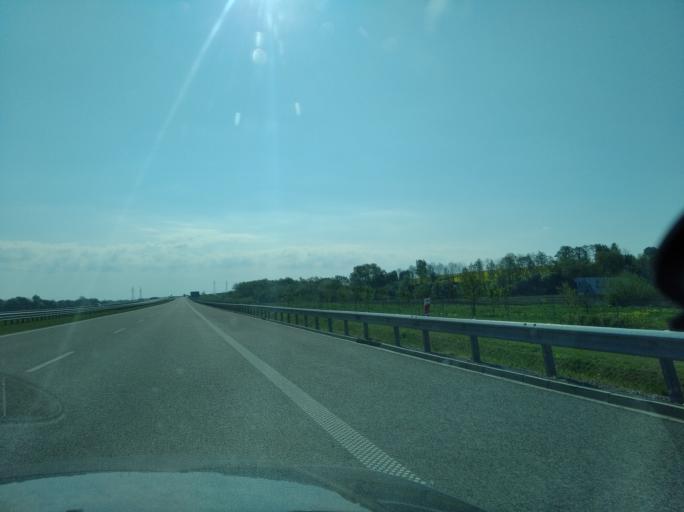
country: PL
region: Subcarpathian Voivodeship
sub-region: Powiat przemyski
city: Orly
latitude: 49.9155
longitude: 22.7749
